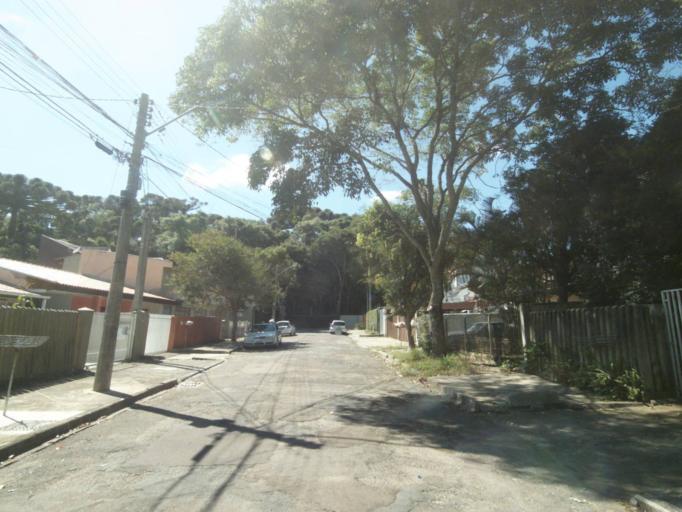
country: BR
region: Parana
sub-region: Pinhais
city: Pinhais
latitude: -25.4359
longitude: -49.2213
